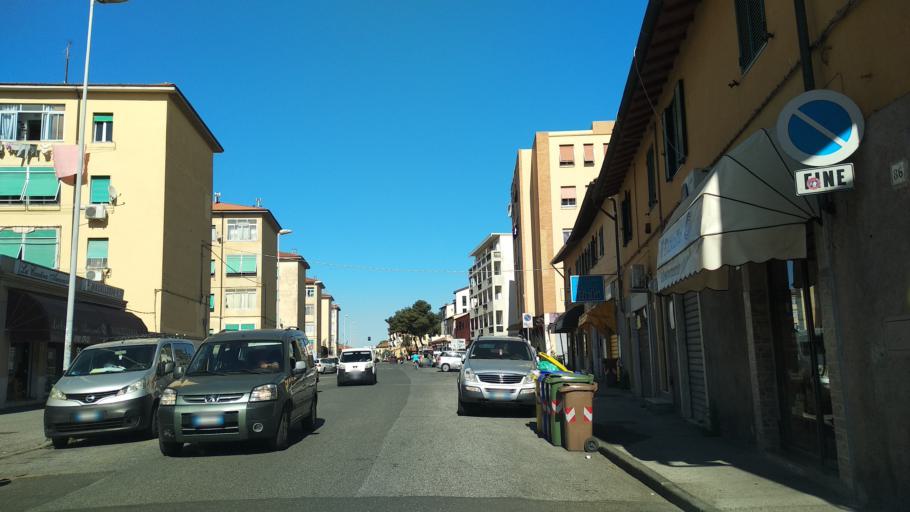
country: IT
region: Tuscany
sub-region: Provincia di Livorno
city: Livorno
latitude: 43.5597
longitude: 10.3302
